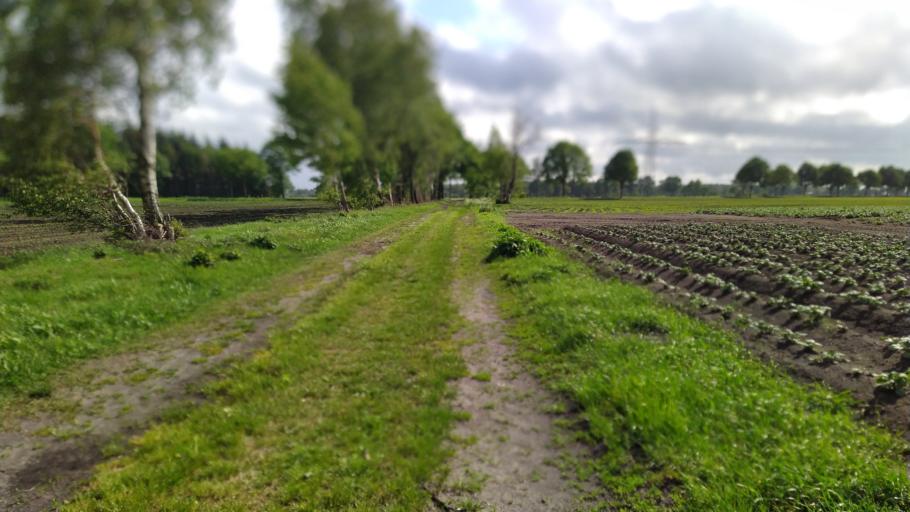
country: DE
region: Lower Saxony
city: Brest
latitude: 53.4545
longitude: 9.4035
